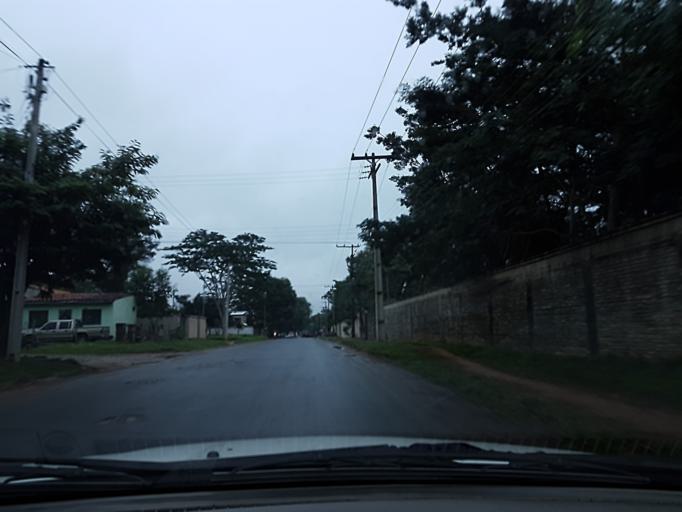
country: PY
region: Central
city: Colonia Mariano Roque Alonso
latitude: -25.2171
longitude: -57.5405
